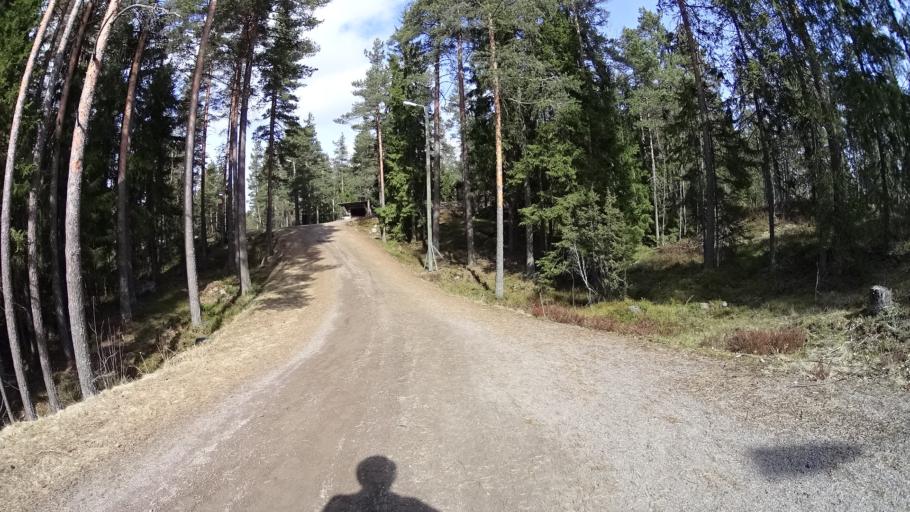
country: FI
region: Uusimaa
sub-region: Helsinki
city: Kilo
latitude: 60.3028
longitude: 24.8137
